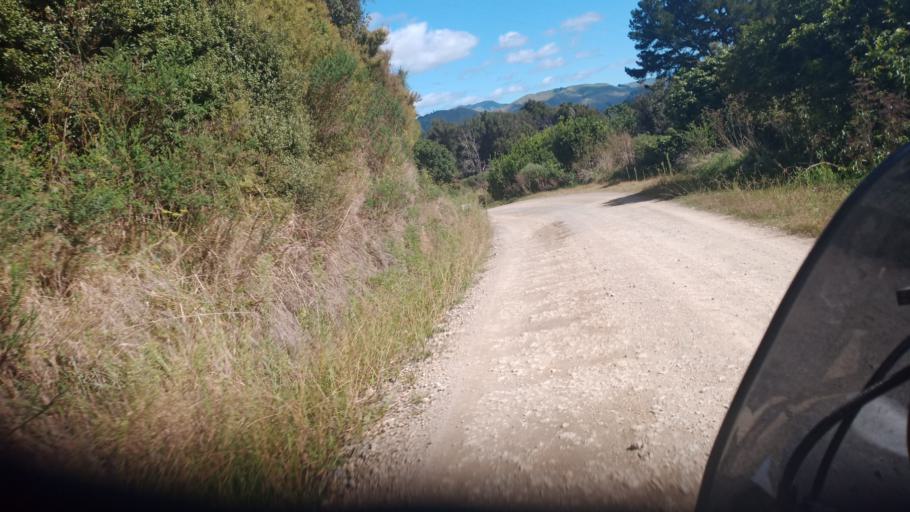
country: NZ
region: Gisborne
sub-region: Gisborne District
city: Gisborne
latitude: -38.3967
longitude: 177.6677
